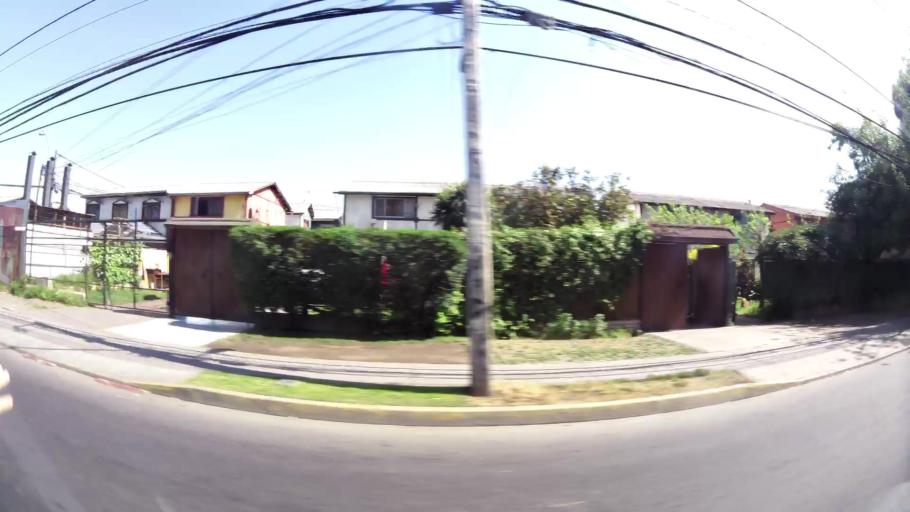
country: CL
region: Santiago Metropolitan
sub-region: Provincia de Santiago
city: Lo Prado
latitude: -33.4738
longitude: -70.7393
